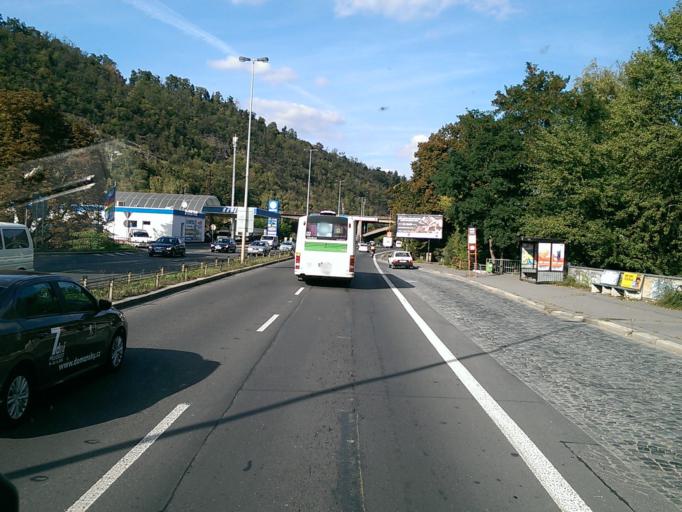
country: CZ
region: Praha
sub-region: Praha 12
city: Modrany
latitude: 50.0248
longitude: 14.3948
